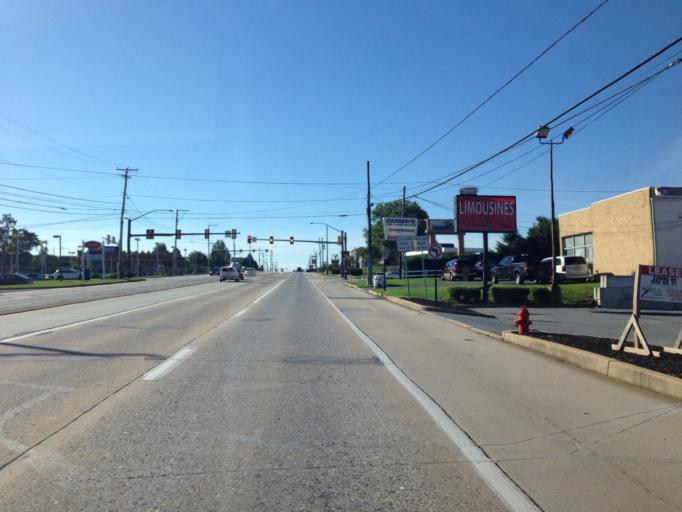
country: US
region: Pennsylvania
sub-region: Lancaster County
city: East Petersburg
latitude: 40.0727
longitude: -76.3350
